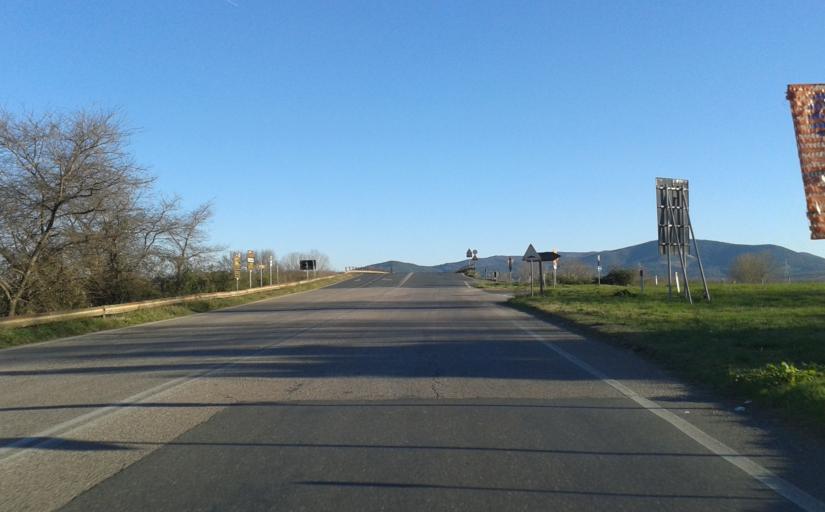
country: IT
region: Tuscany
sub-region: Provincia di Livorno
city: Livorno
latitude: 43.5748
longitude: 10.3449
